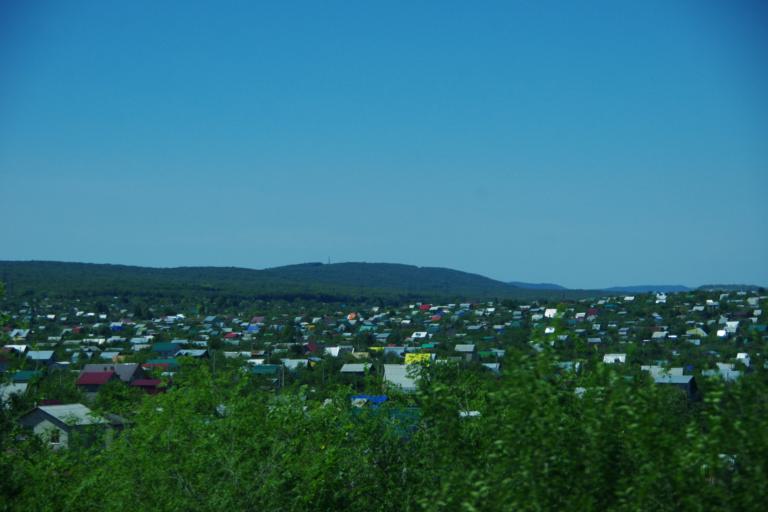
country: RU
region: Samara
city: Novosemeykino
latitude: 53.4085
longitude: 50.3367
